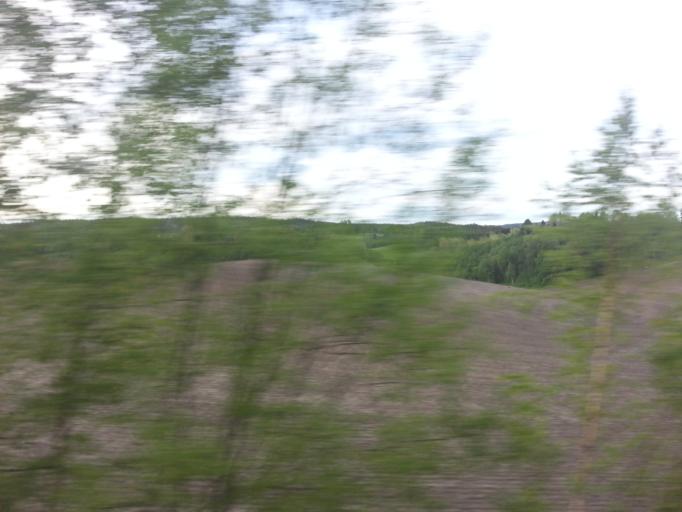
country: NO
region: Akershus
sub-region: Eidsvoll
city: Eidsvoll
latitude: 60.3097
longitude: 11.2245
